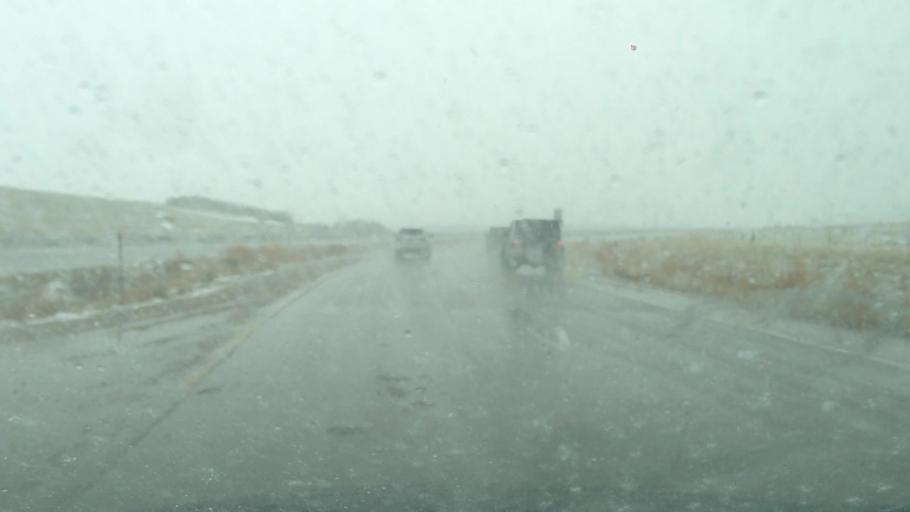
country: US
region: Colorado
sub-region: Park County
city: Castle Pines North
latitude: 39.4710
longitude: -104.8642
